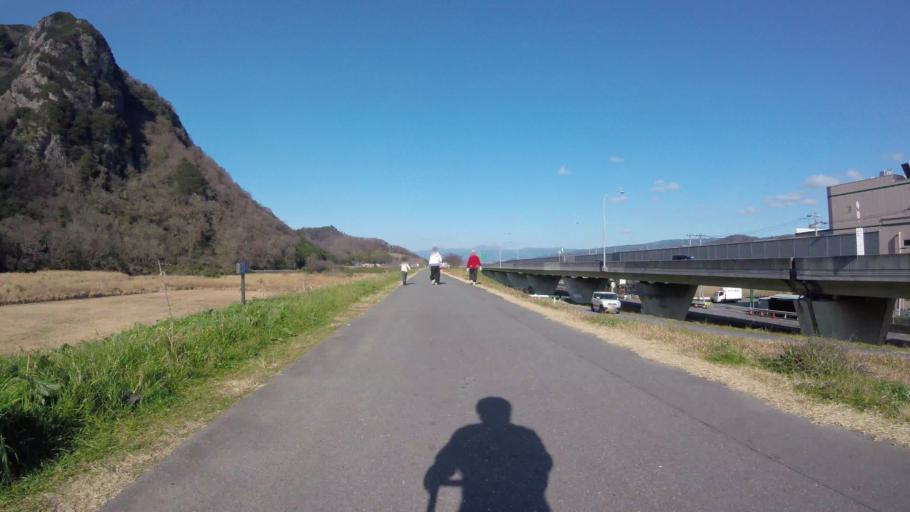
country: JP
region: Shizuoka
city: Mishima
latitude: 35.0003
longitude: 138.9351
